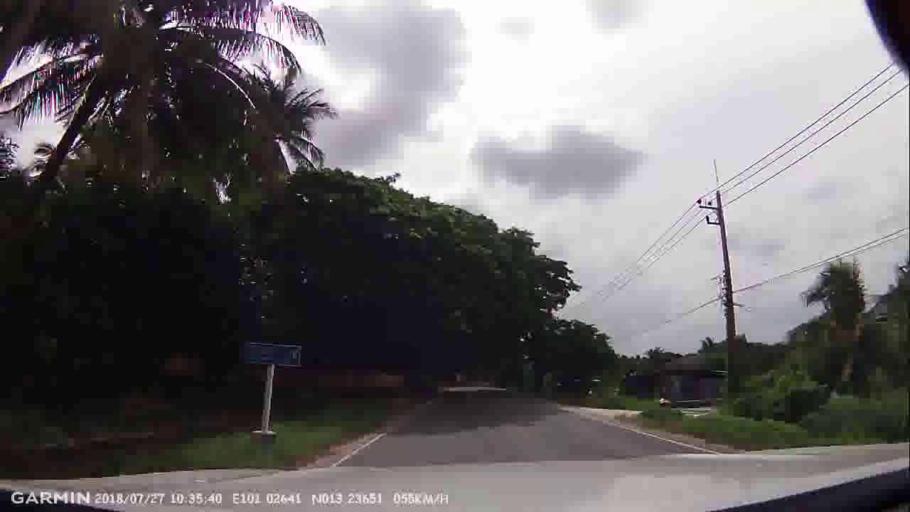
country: TH
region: Chon Buri
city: Ban Bueng
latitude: 13.2365
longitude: 101.0265
